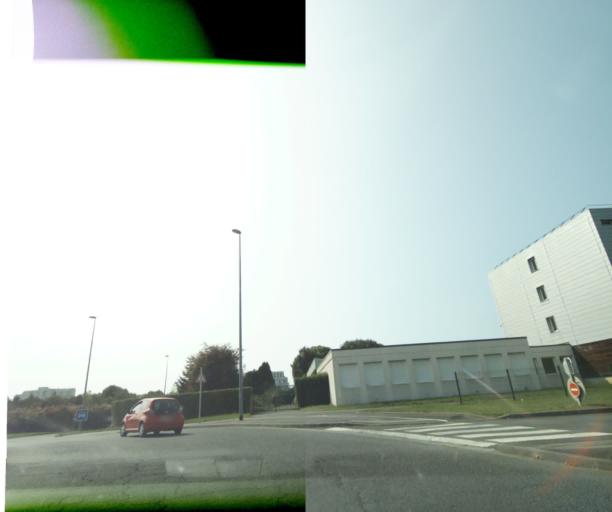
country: FR
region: Lower Normandy
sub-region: Departement du Calvados
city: Caen
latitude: 49.2003
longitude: -0.3442
